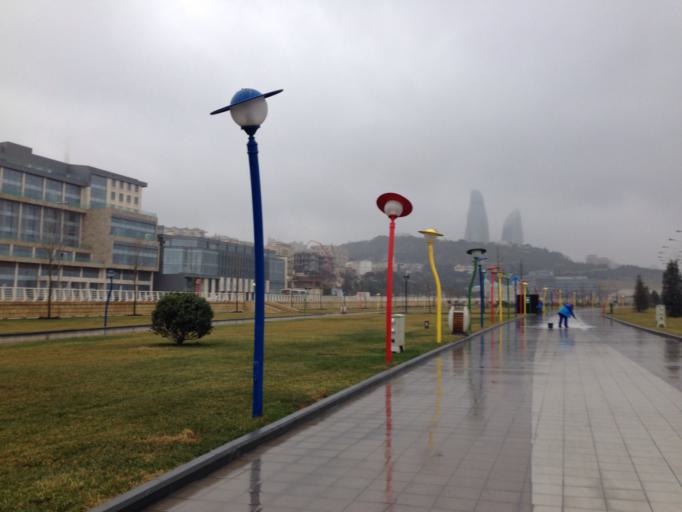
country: AZ
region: Baki
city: Badamdar
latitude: 40.3488
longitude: 49.8380
